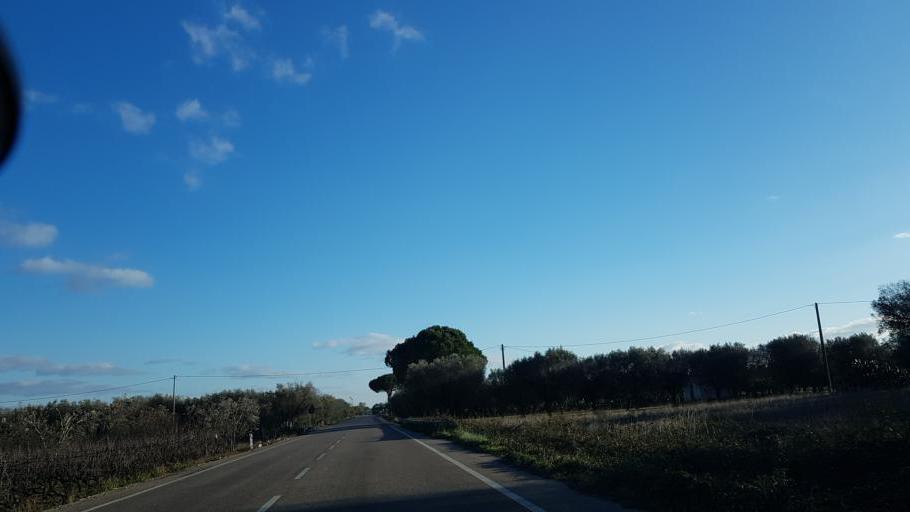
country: IT
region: Apulia
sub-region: Provincia di Lecce
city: Squinzano
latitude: 40.4538
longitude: 18.0259
